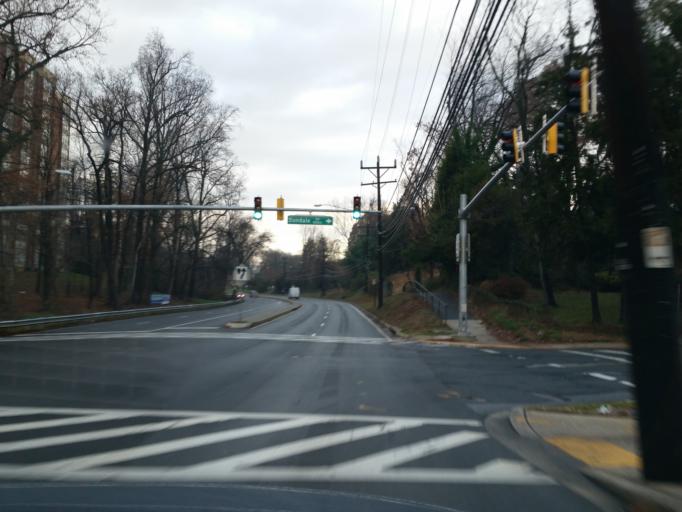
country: US
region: Maryland
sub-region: Montgomery County
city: Silver Spring
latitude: 38.9950
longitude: -77.0454
